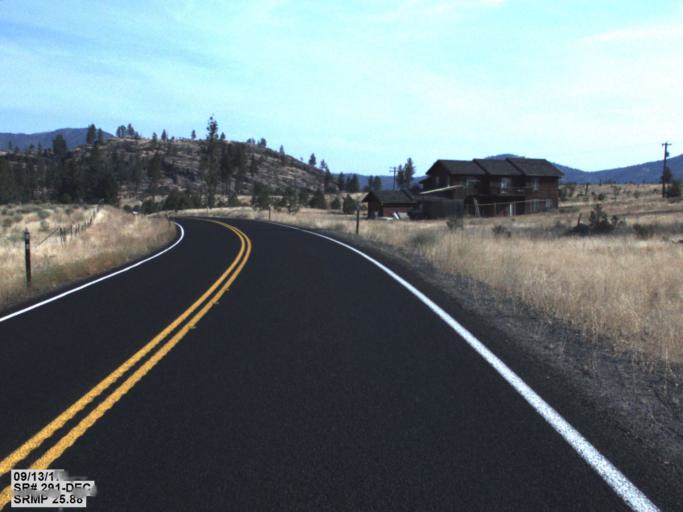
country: US
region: Washington
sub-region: Spokane County
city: Airway Heights
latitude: 47.8533
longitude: -117.7133
